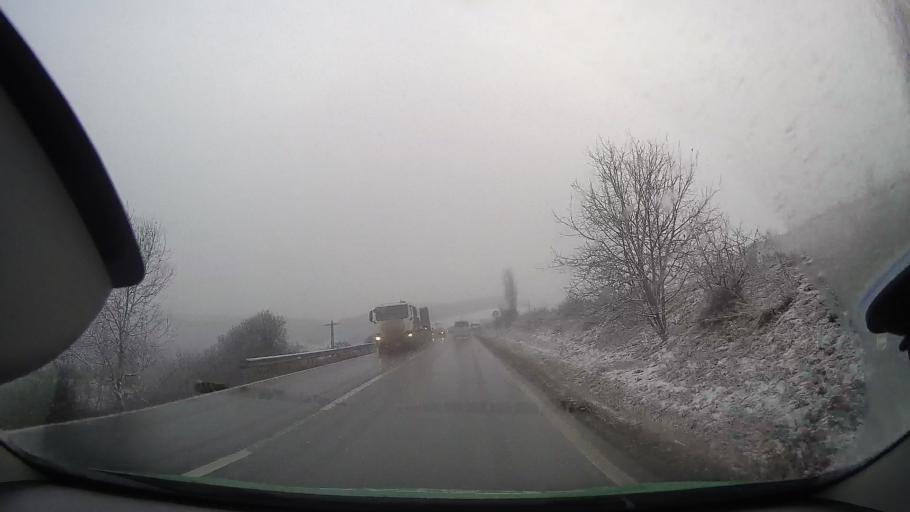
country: RO
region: Mures
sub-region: Comuna Bagaciu
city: Delenii
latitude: 46.2636
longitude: 24.3013
